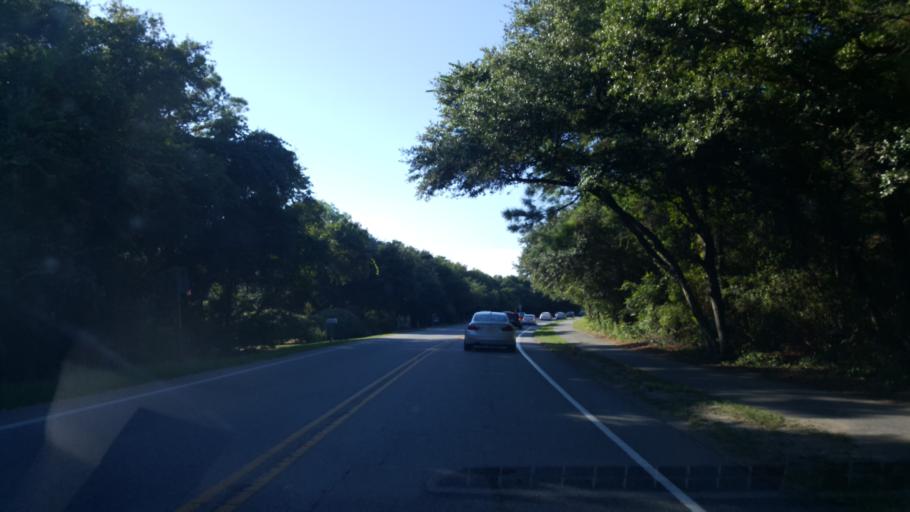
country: US
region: North Carolina
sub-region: Dare County
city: Southern Shores
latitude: 36.1333
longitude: -75.7344
